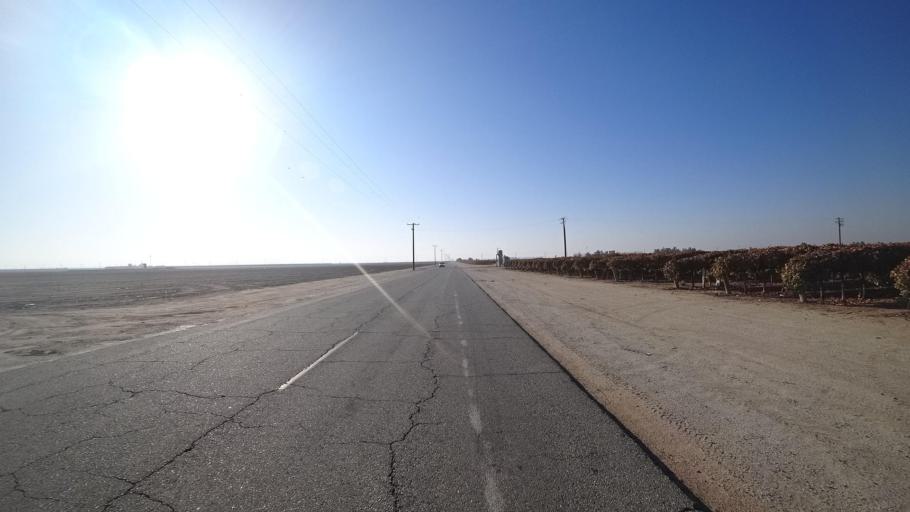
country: US
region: California
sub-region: Tulare County
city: Richgrove
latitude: 35.7833
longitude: -119.1697
